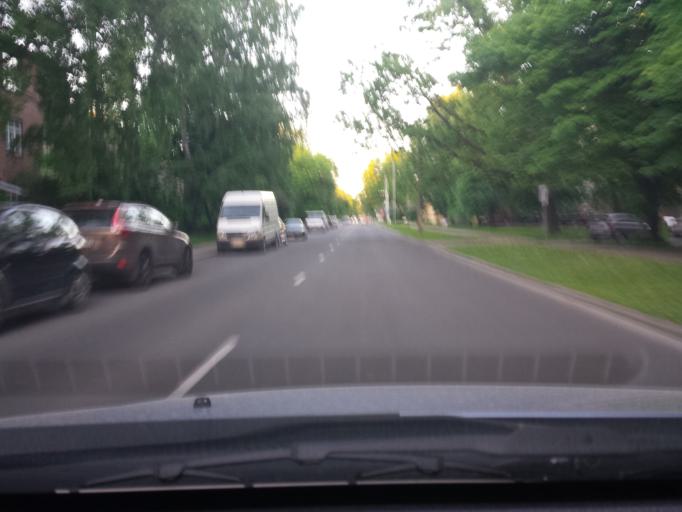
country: LV
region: Riga
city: Jaunciems
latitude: 56.9696
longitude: 24.1851
